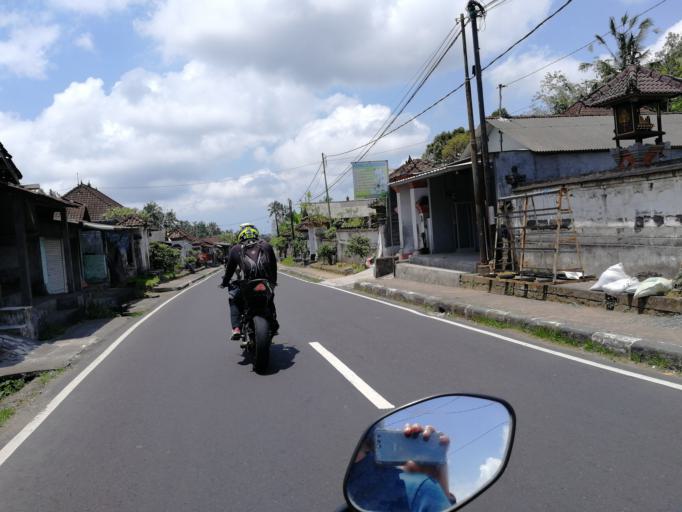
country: ID
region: Bali
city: Banjar Brahmanabukit
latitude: -8.4503
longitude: 115.3864
